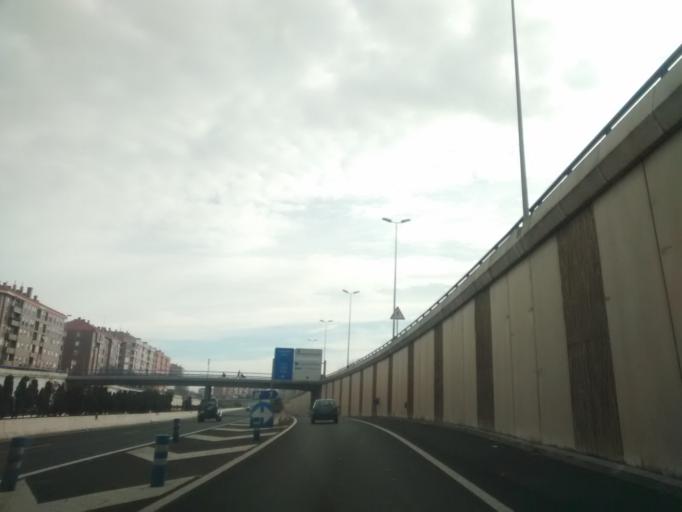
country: ES
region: La Rioja
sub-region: Provincia de La Rioja
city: Logrono
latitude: 42.4537
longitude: -2.4371
